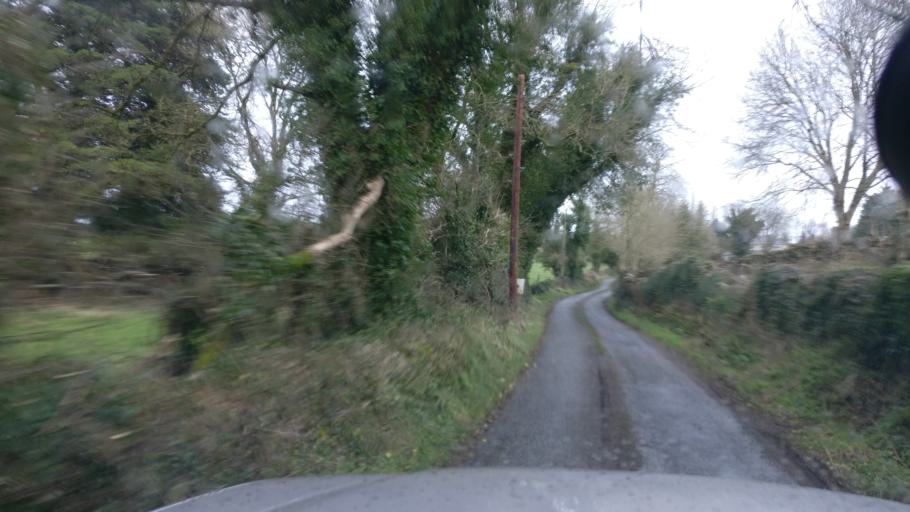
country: IE
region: Connaught
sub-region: County Galway
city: Loughrea
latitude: 53.1812
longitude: -8.6062
